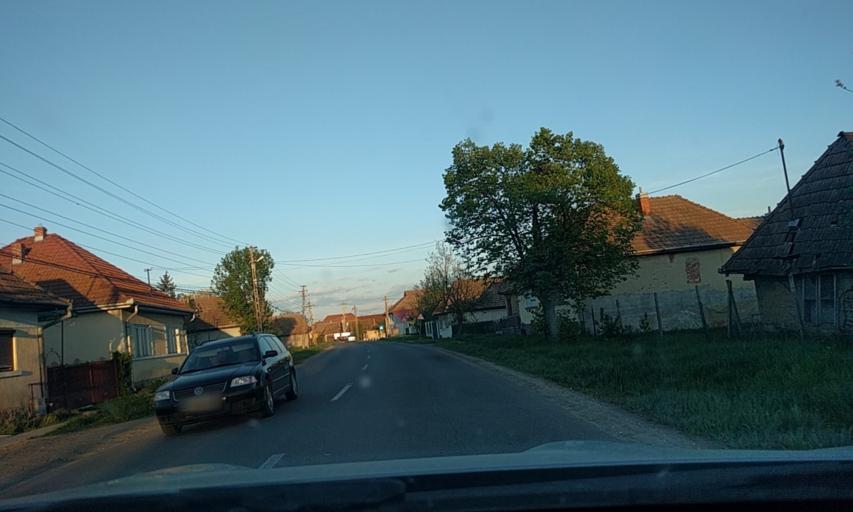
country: RO
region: Mures
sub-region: Comuna Craciunesti
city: Craciunesti
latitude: 46.4805
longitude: 24.5883
